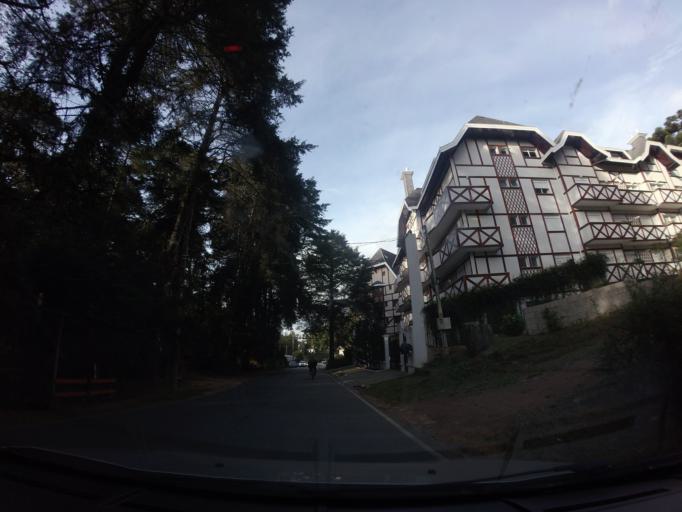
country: BR
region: Sao Paulo
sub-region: Campos Do Jordao
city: Campos do Jordao
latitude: -22.7327
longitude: -45.5703
